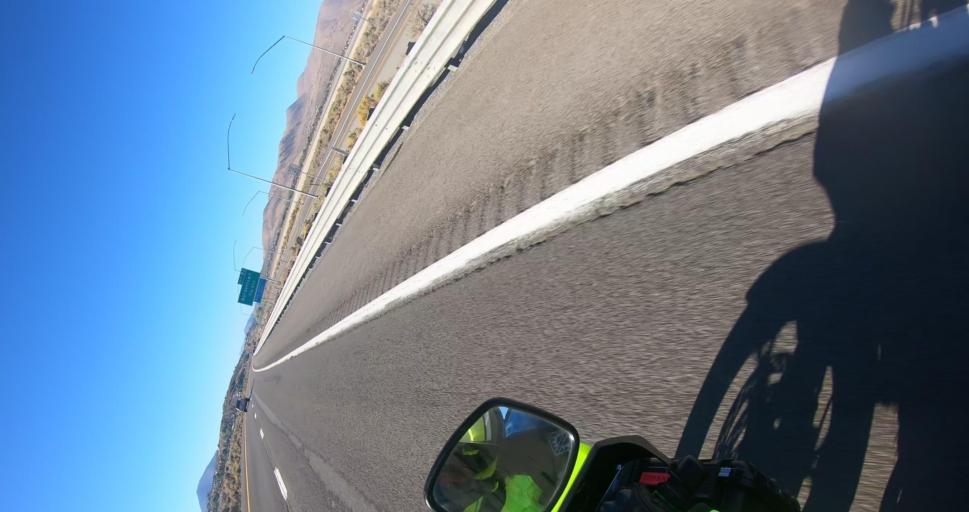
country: US
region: Nevada
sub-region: Washoe County
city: Cold Springs
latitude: 39.6540
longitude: -119.9835
